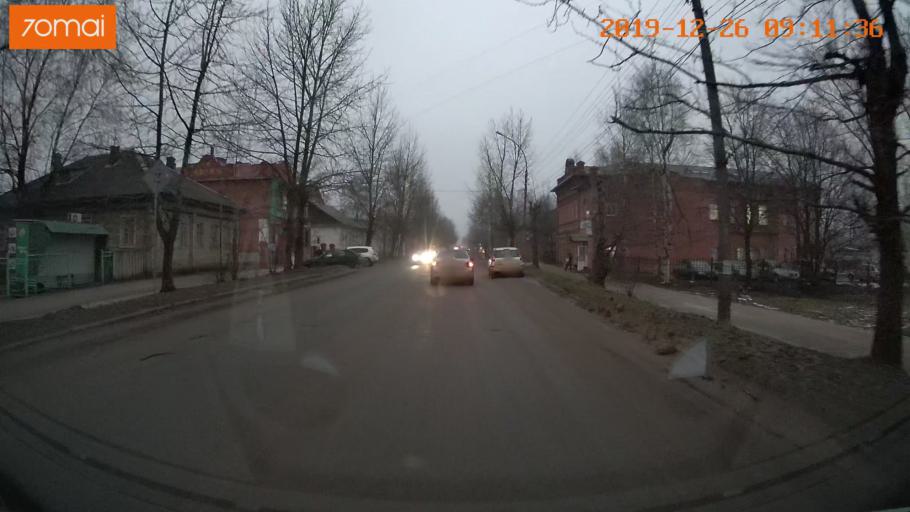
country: RU
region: Vologda
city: Gryazovets
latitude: 58.8770
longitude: 40.2528
